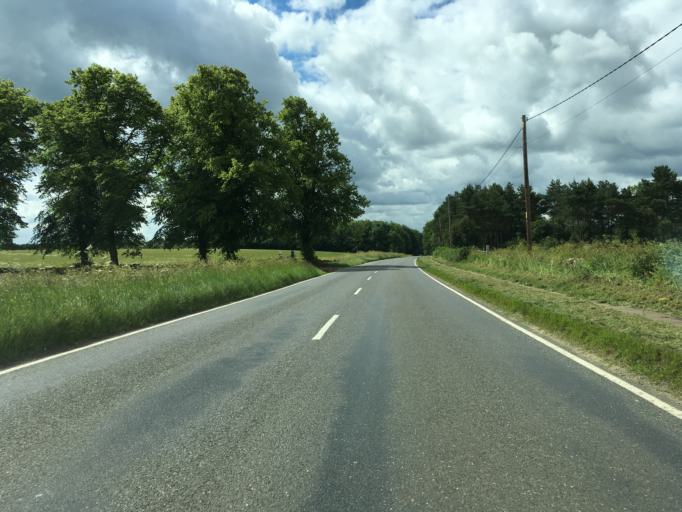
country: GB
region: England
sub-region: Oxfordshire
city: Chipping Norton
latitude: 51.9245
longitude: -1.5412
